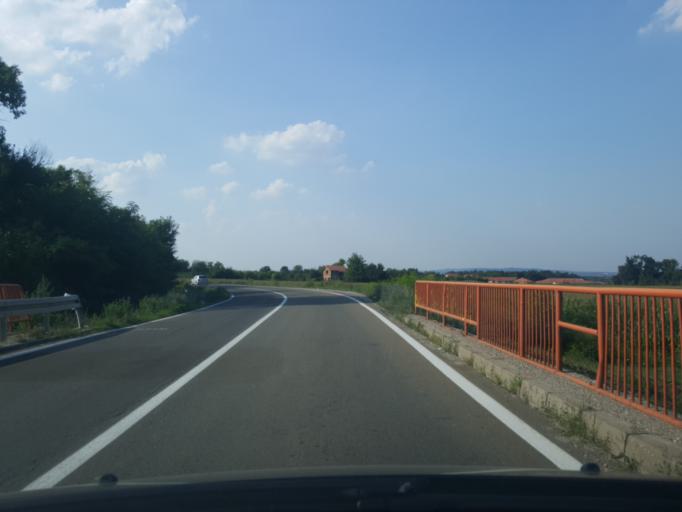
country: RS
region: Central Serbia
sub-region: Belgrade
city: Mladenovac
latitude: 44.3780
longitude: 20.6758
